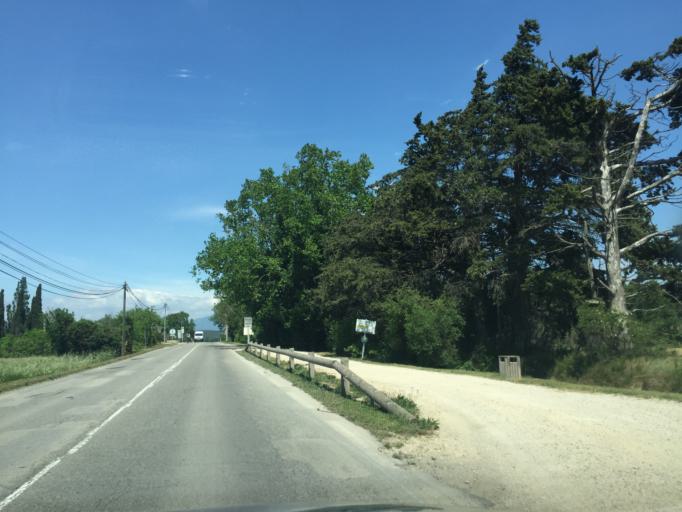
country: FR
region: Provence-Alpes-Cote d'Azur
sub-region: Departement du Vaucluse
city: Pernes-les-Fontaines
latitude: 44.0047
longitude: 5.0635
